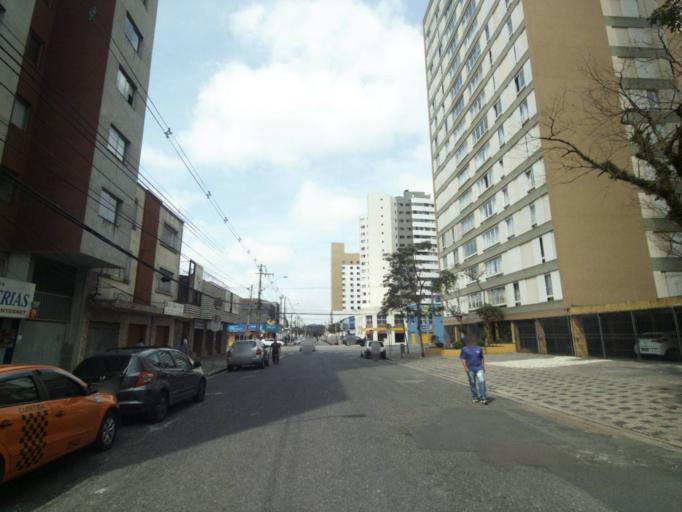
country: BR
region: Parana
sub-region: Curitiba
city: Curitiba
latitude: -25.4329
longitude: -49.2604
